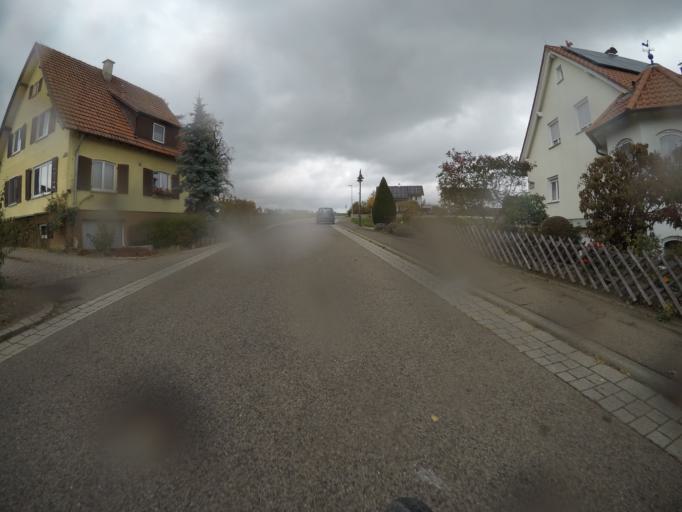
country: DE
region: Baden-Wuerttemberg
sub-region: Regierungsbezirk Stuttgart
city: Herrenberg
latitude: 48.6092
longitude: 8.8578
